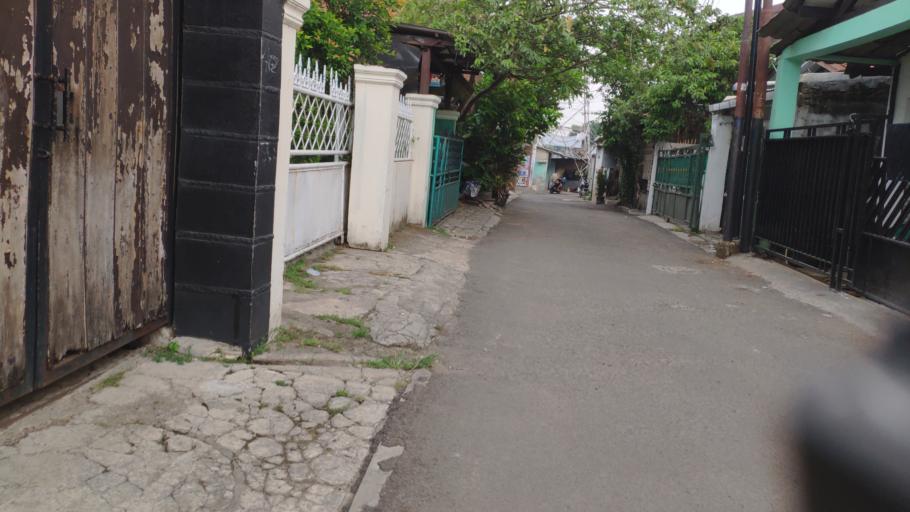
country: ID
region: West Java
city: Depok
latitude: -6.3173
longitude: 106.8274
